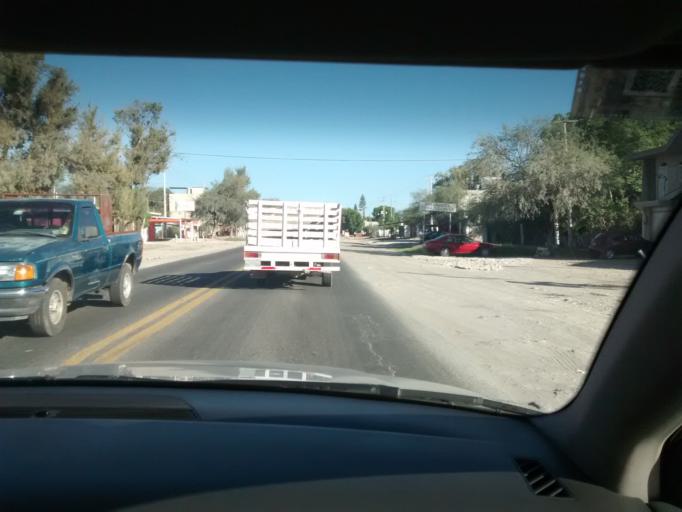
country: MX
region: Puebla
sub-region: Tehuacan
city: Magdalena Cuayucatepec
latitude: 18.5092
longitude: -97.4895
